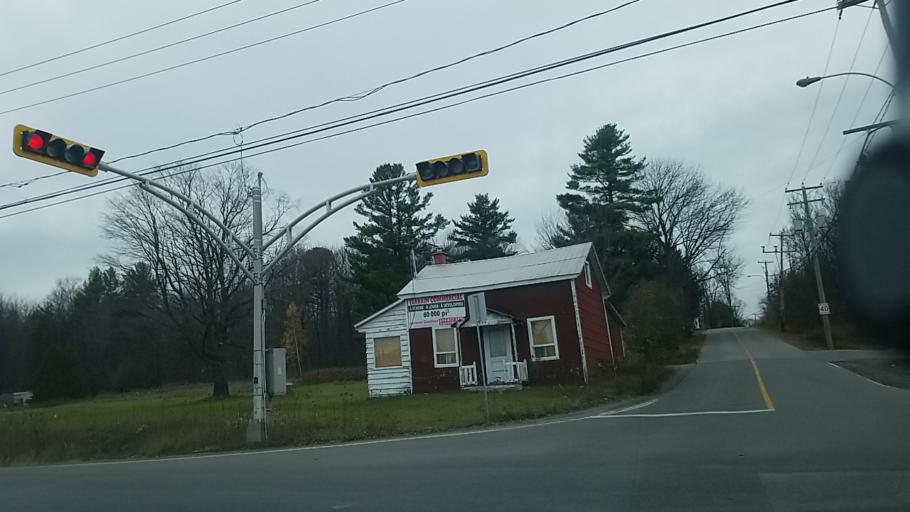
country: CA
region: Quebec
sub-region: Laurentides
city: Saint-Jerome
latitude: 45.7900
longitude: -74.0535
